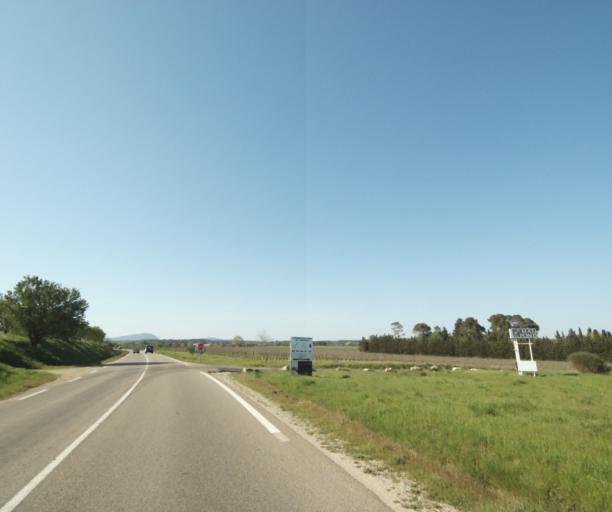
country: FR
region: Languedoc-Roussillon
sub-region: Departement de l'Herault
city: Jacou
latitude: 43.6644
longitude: 3.9245
